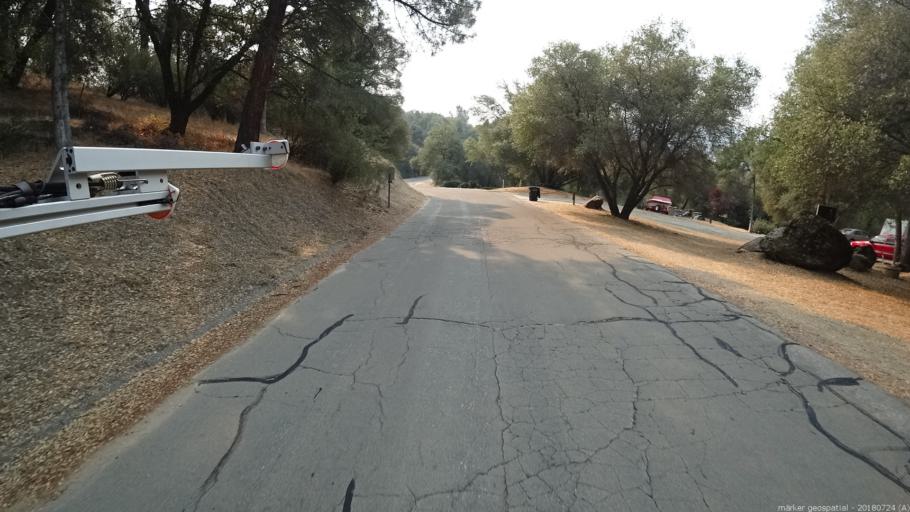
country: US
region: California
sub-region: Madera County
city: Oakhurst
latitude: 37.3140
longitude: -119.6353
